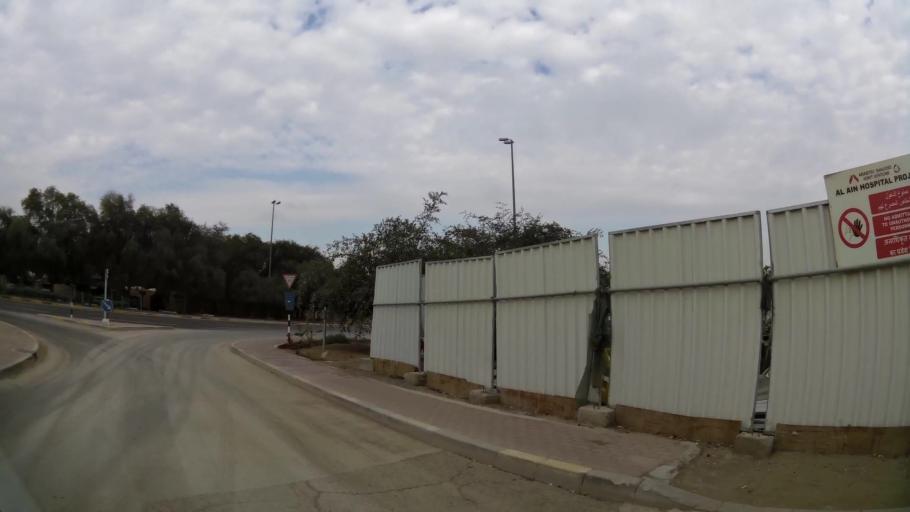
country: AE
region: Abu Dhabi
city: Al Ain
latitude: 24.2287
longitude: 55.7311
